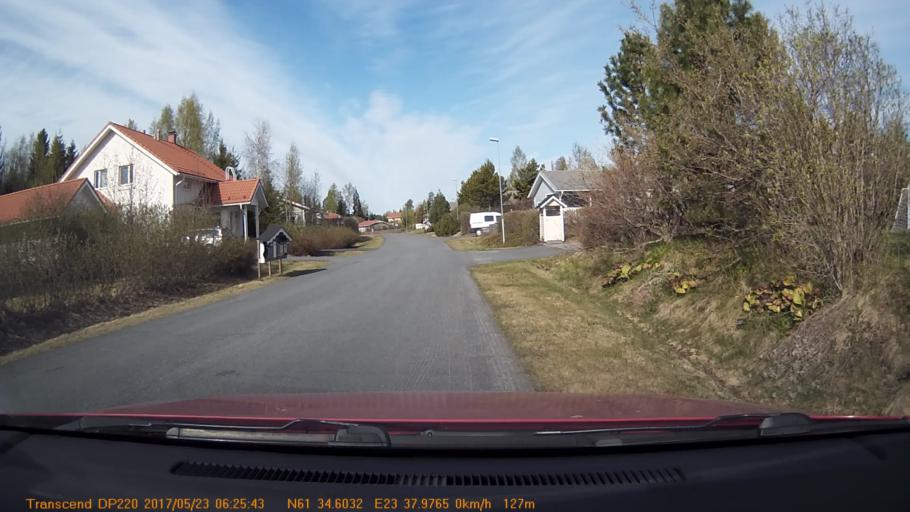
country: FI
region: Pirkanmaa
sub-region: Tampere
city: Yloejaervi
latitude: 61.5768
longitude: 23.6330
